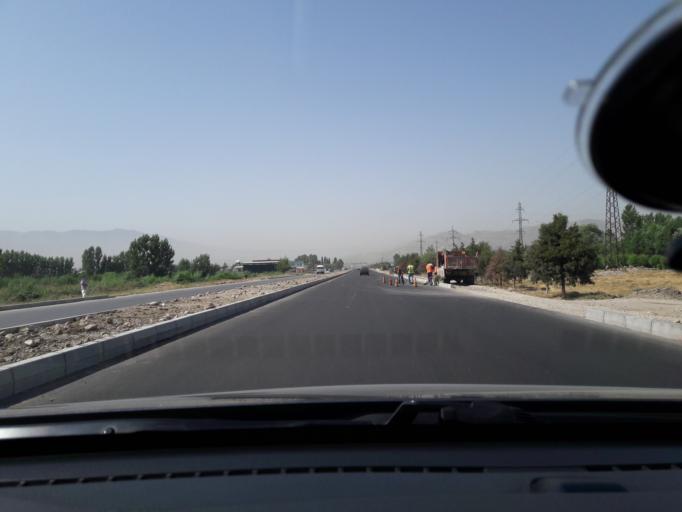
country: TJ
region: Dushanbe
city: Dushanbe
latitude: 38.4862
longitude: 68.7493
